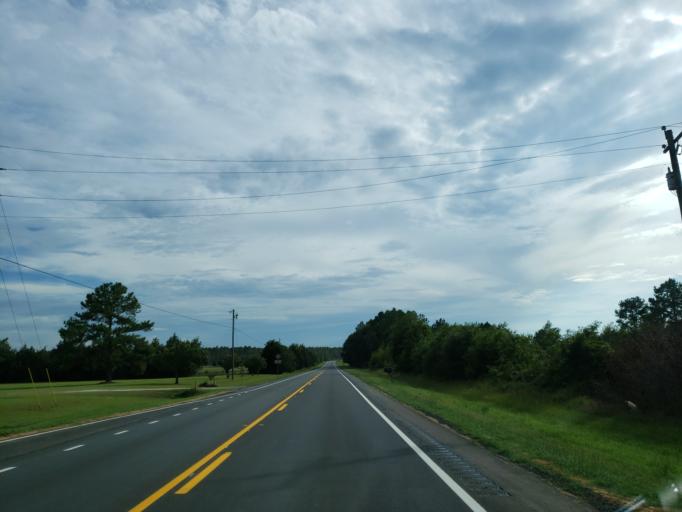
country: US
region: Georgia
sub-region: Irwin County
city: Ocilla
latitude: 31.5464
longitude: -83.3801
